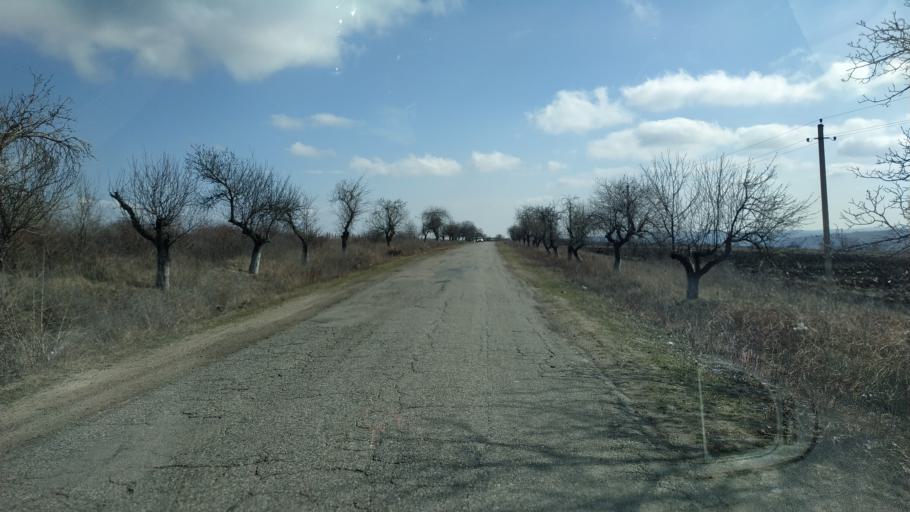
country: MD
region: Hincesti
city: Hincesti
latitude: 46.8515
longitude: 28.6471
